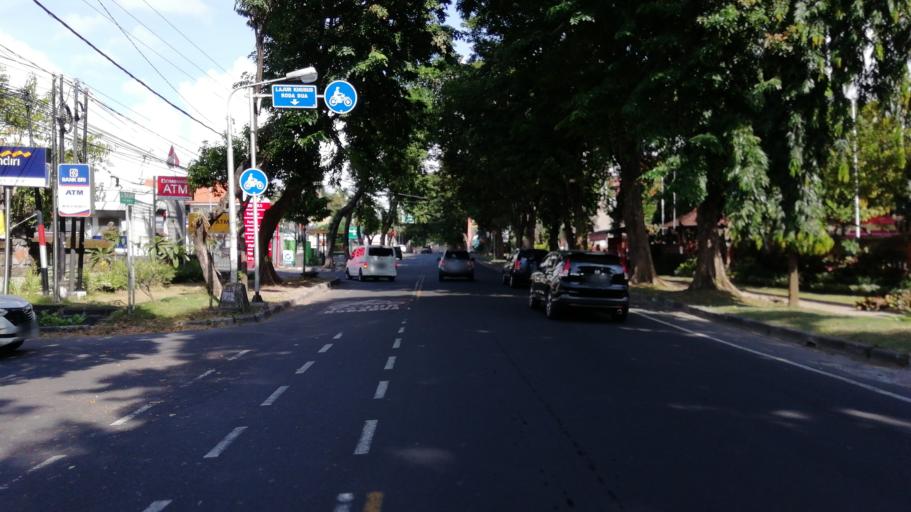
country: ID
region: Bali
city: Denpasar
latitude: -8.6729
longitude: 115.2265
